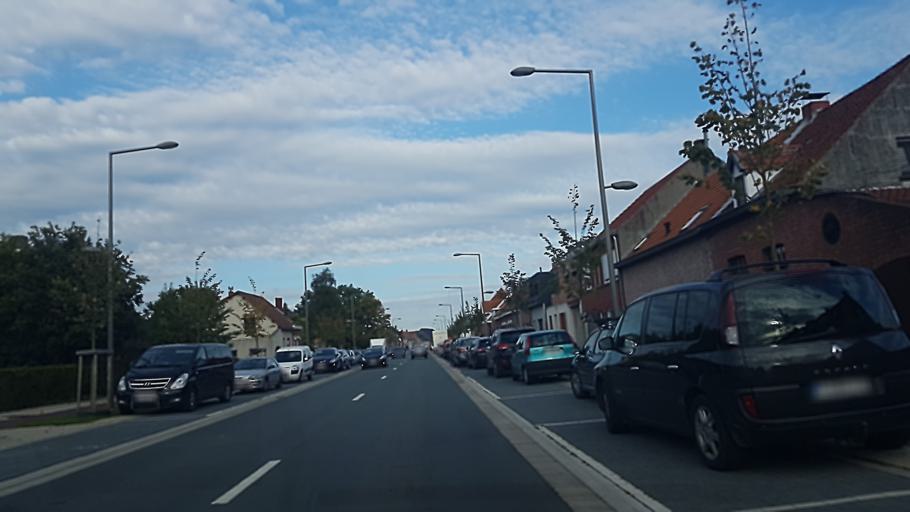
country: BE
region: Flanders
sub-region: Provincie Antwerpen
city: Stabroek
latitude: 51.3459
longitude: 4.3946
